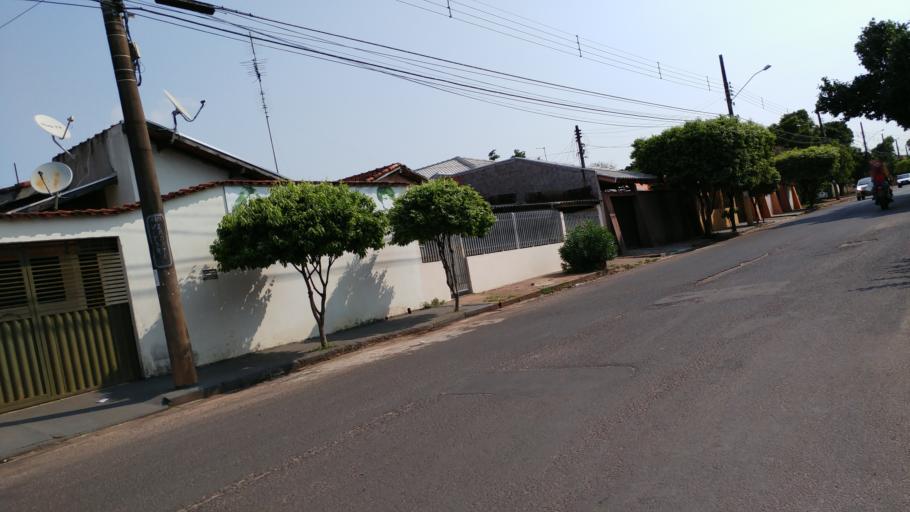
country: BR
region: Sao Paulo
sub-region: Paraguacu Paulista
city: Paraguacu Paulista
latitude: -22.4271
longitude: -50.5797
